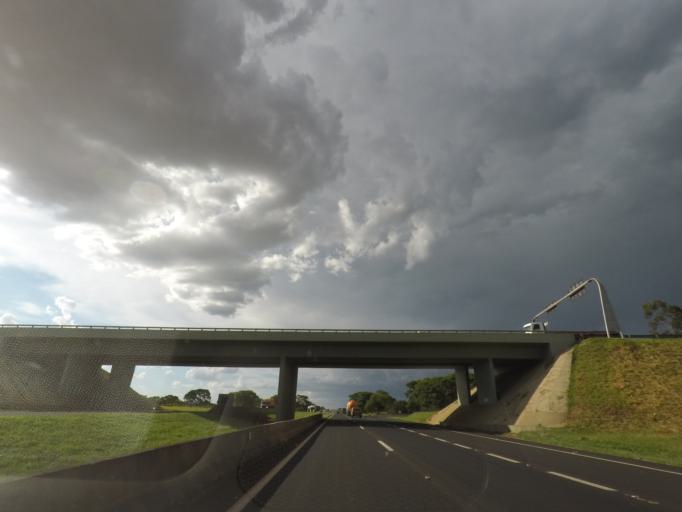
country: BR
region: Sao Paulo
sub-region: Ribeirao Preto
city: Ribeirao Preto
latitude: -21.1130
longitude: -47.7800
